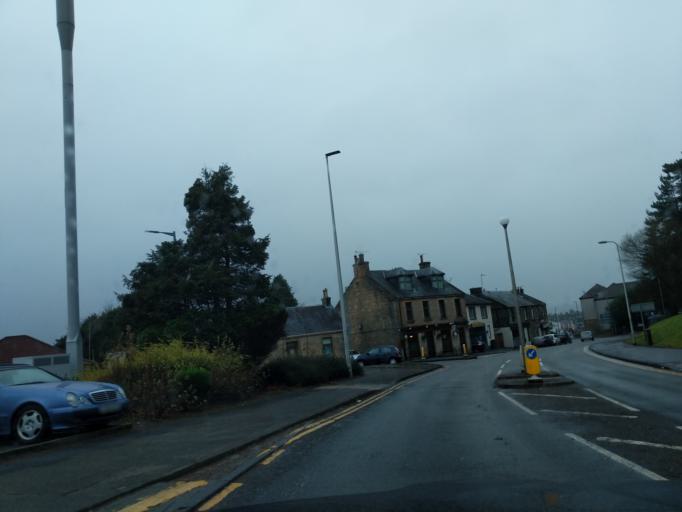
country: GB
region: Scotland
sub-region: Falkirk
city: Falkirk
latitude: 55.9935
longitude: -3.7891
